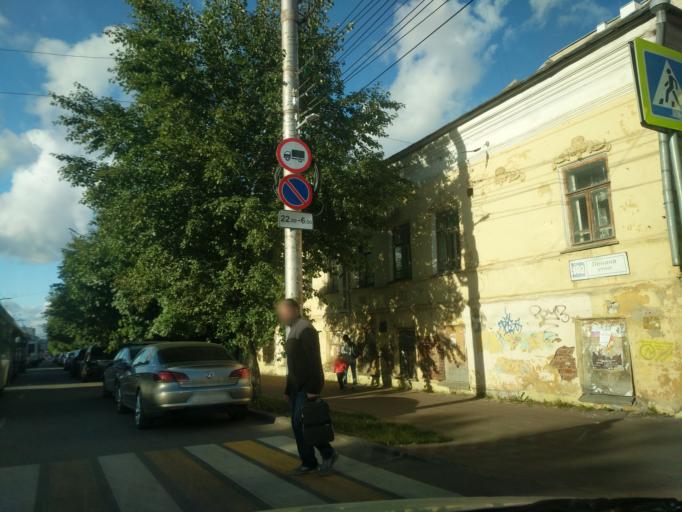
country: RU
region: Kirov
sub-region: Kirovo-Chepetskiy Rayon
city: Kirov
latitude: 58.5963
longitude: 49.6818
